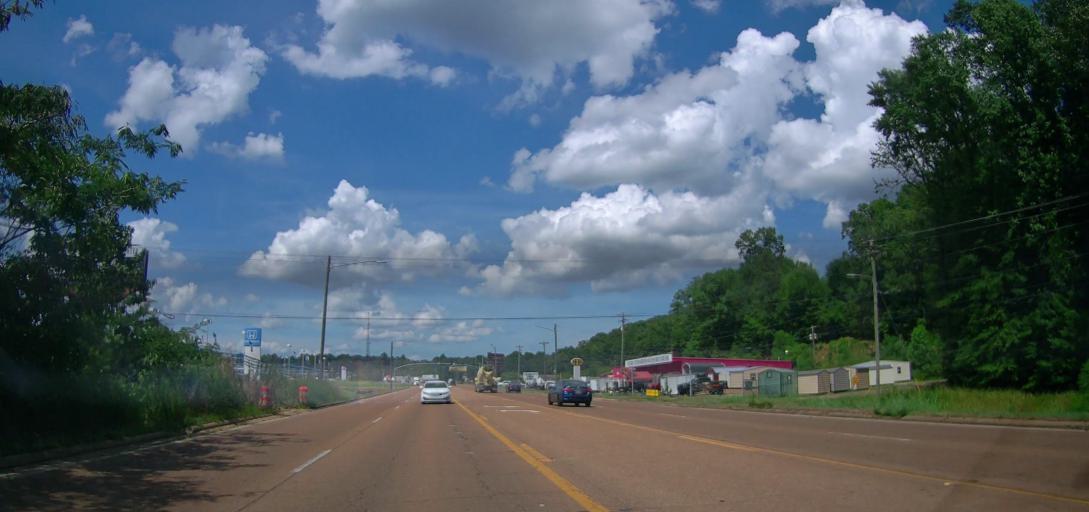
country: US
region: Mississippi
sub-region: Lowndes County
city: Columbus
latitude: 33.5451
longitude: -88.4355
